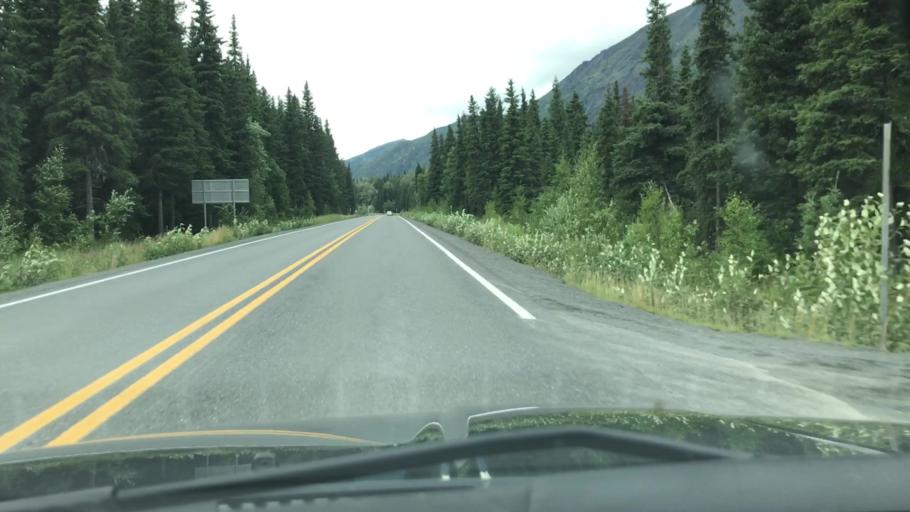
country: US
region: Alaska
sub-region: Kenai Peninsula Borough
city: Seward
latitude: 60.4829
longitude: -149.9377
